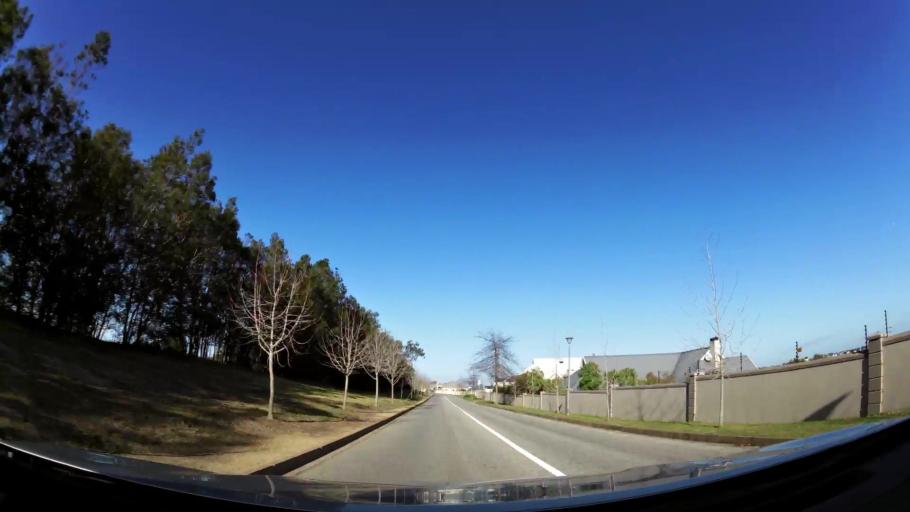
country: ZA
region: Western Cape
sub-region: Eden District Municipality
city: George
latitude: -33.9637
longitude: 22.4396
